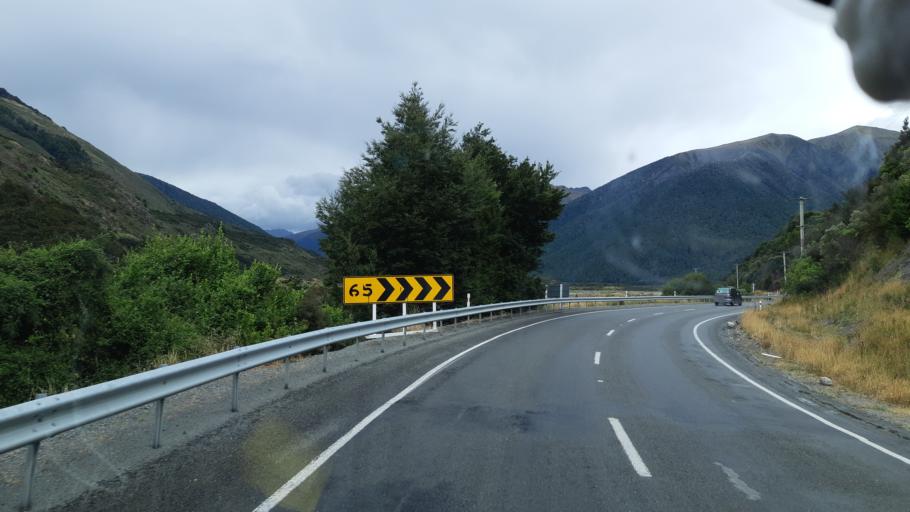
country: NZ
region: Canterbury
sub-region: Hurunui District
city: Amberley
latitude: -42.5642
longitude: 172.3545
